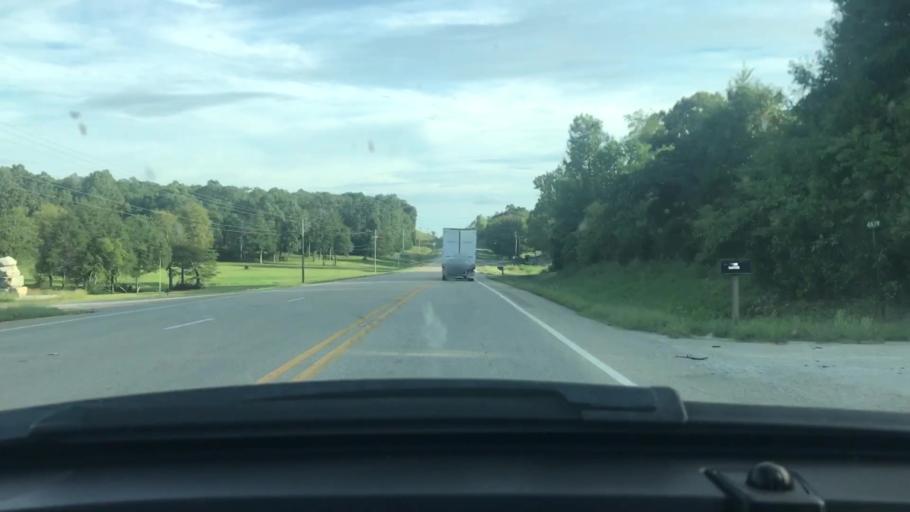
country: US
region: Arkansas
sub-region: Lawrence County
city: Hoxie
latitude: 36.1534
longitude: -91.1612
